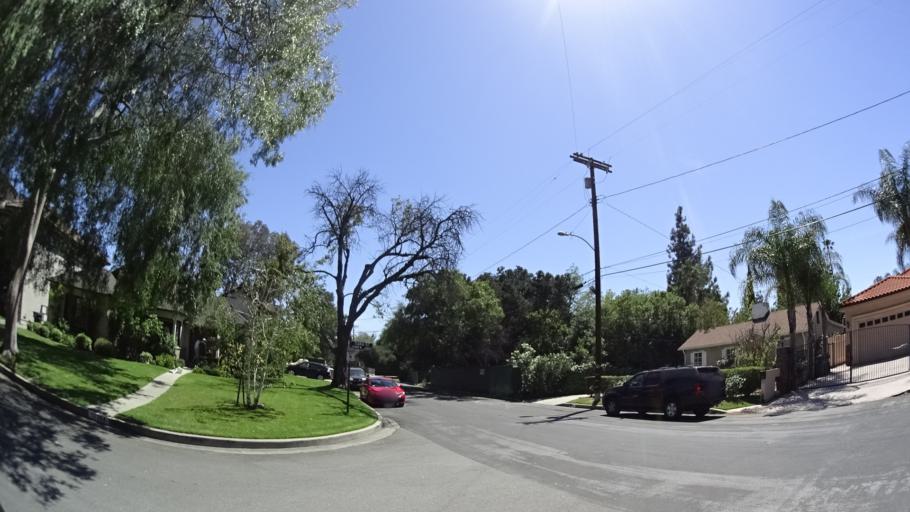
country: US
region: California
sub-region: Los Angeles County
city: North Hollywood
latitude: 34.1784
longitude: -118.4030
